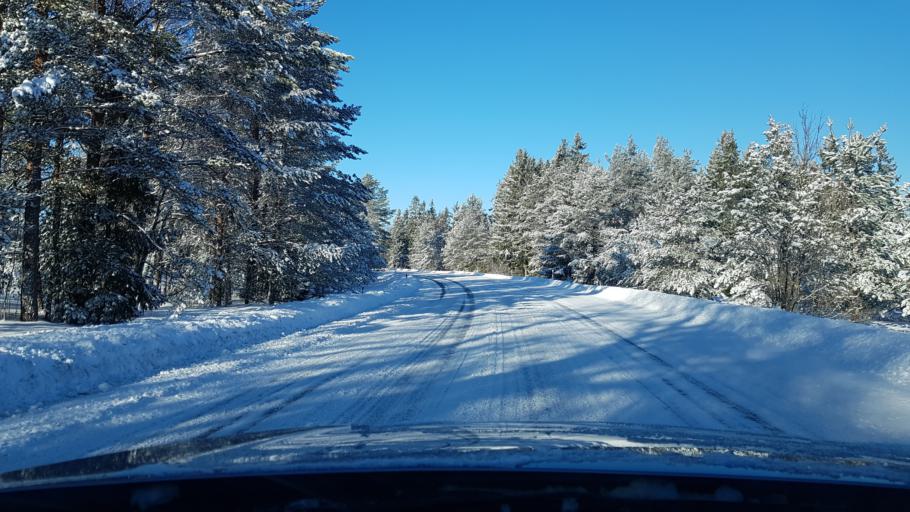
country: EE
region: Hiiumaa
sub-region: Kaerdla linn
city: Kardla
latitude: 58.9356
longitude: 22.7819
